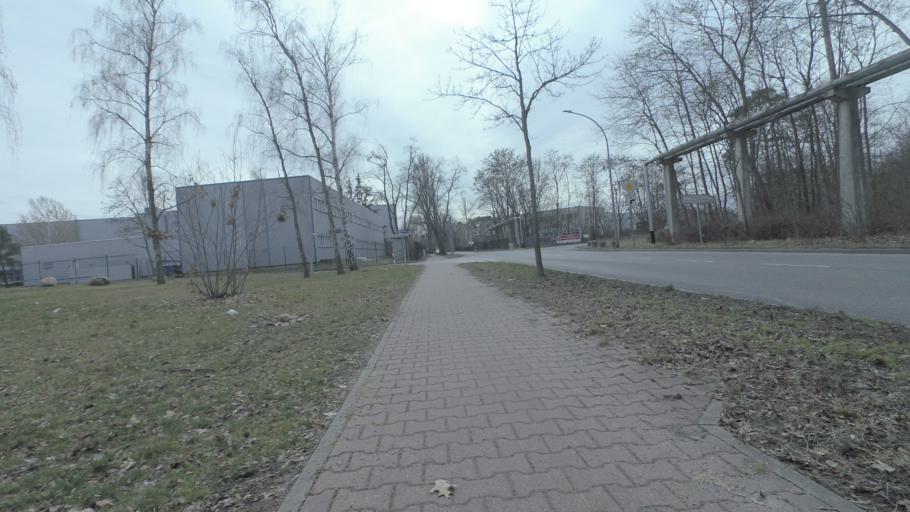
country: DE
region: Brandenburg
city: Ludwigsfelde
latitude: 52.3292
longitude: 13.2705
